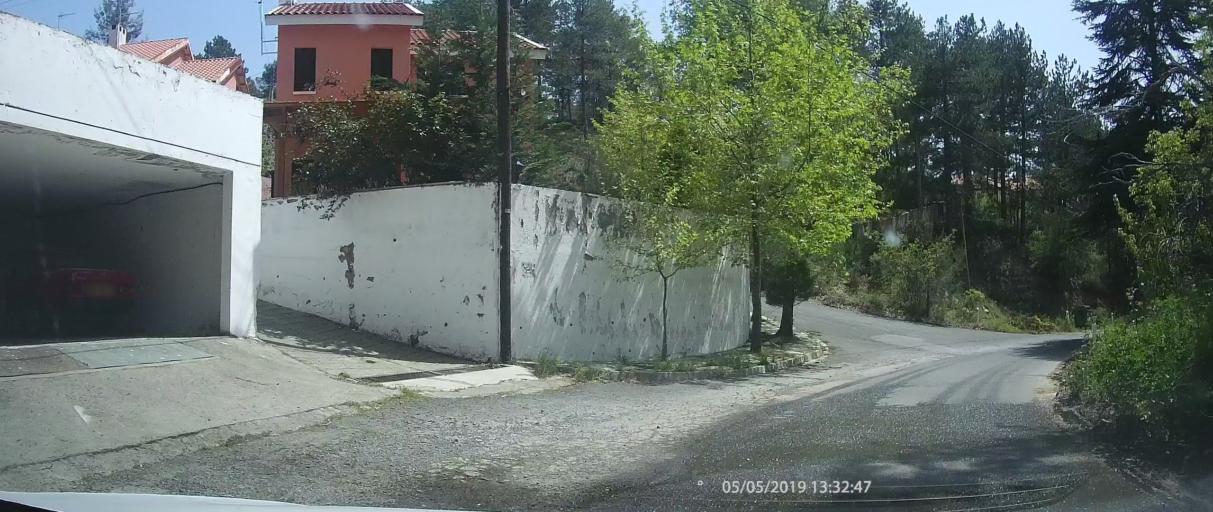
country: CY
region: Lefkosia
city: Kakopetria
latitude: 34.8886
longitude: 32.8552
